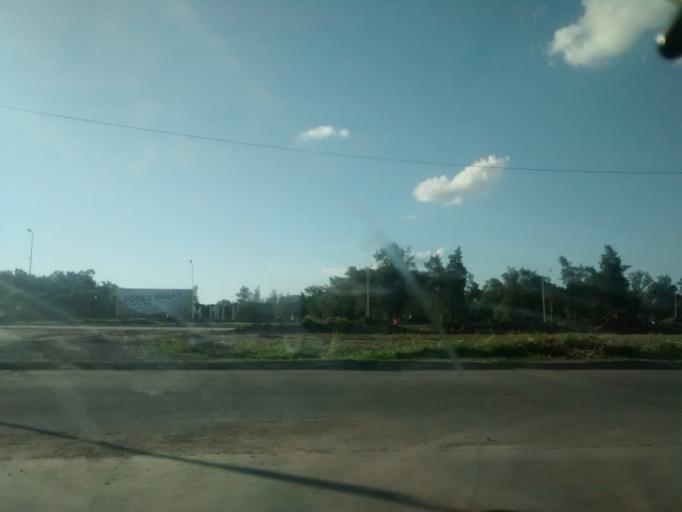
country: AR
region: Chaco
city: Fontana
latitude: -27.4462
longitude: -59.0228
